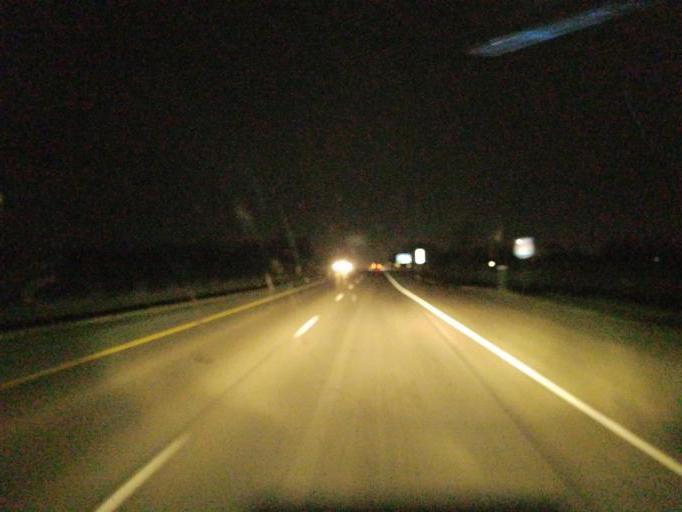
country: US
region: Iowa
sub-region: Dallas County
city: Waukee
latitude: 41.5758
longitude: -93.8405
